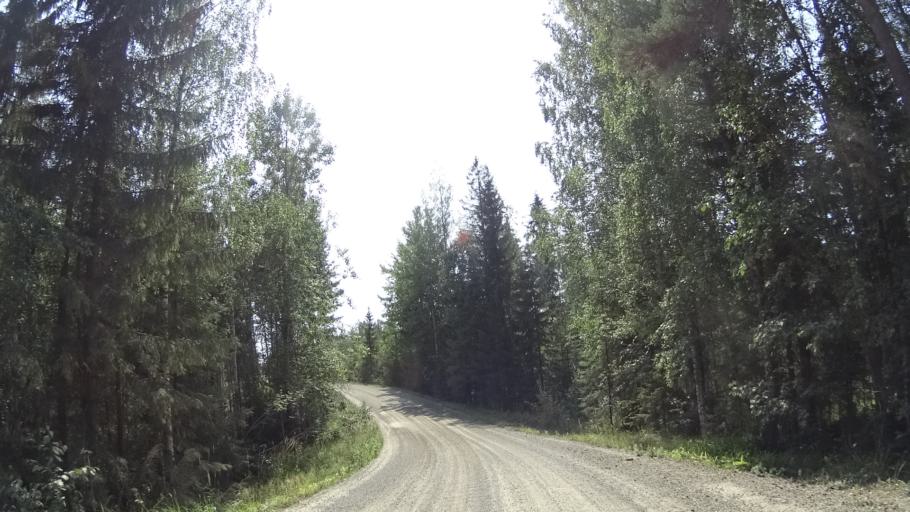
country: FI
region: Central Finland
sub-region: Jaemsae
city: Jaemsae
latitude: 61.7511
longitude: 24.8912
